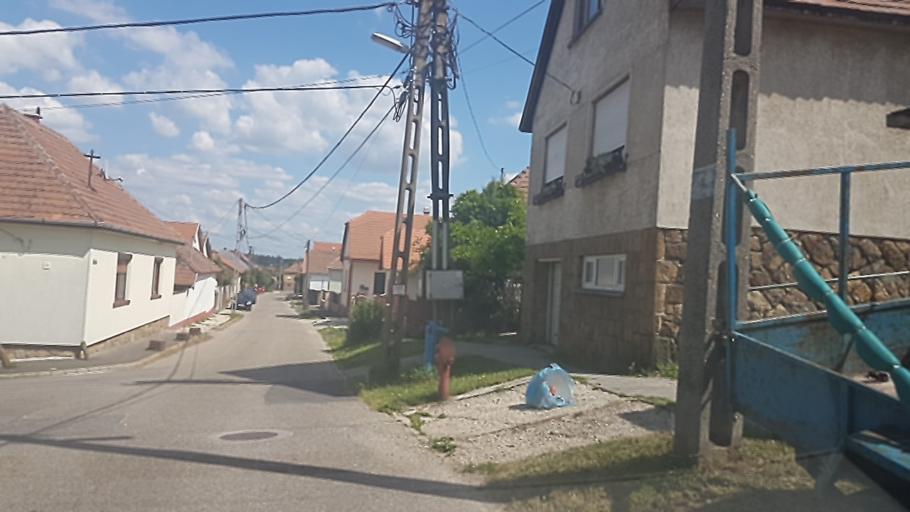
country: HU
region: Pest
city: Pilisszentivan
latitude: 47.6100
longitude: 18.8919
